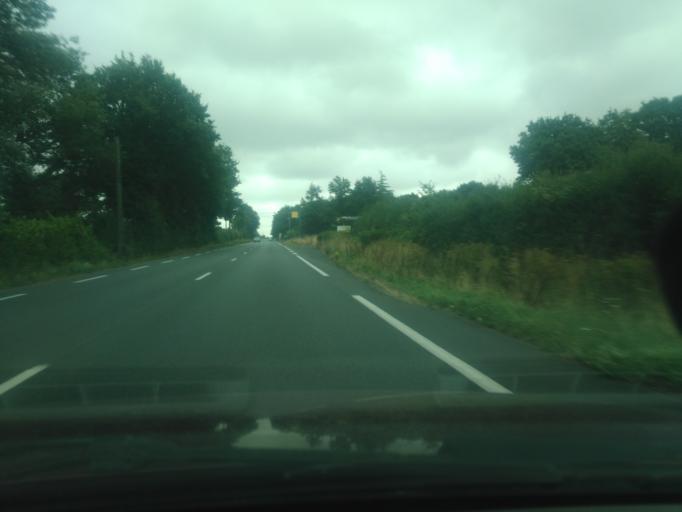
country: FR
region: Pays de la Loire
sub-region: Departement de la Vendee
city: La Ferriere
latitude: 46.6950
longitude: -1.3598
